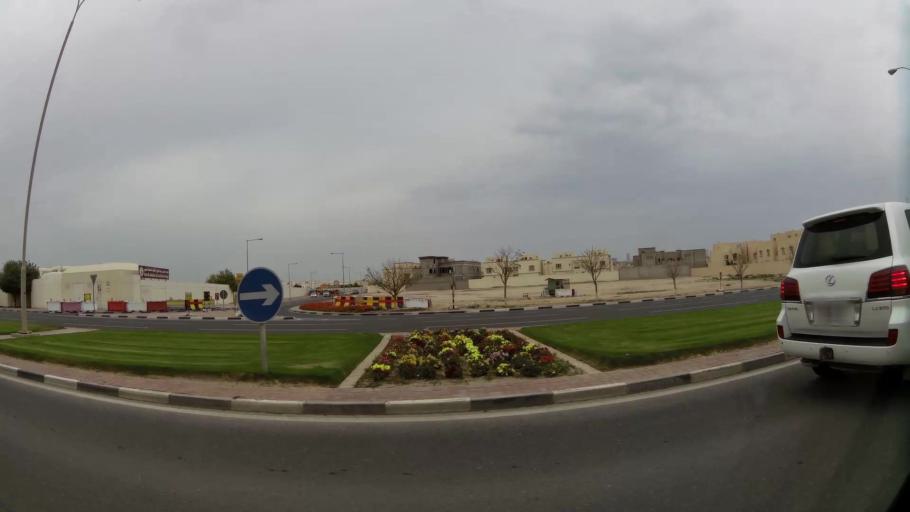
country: QA
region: Baladiyat ad Dawhah
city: Doha
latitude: 25.3305
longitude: 51.4827
